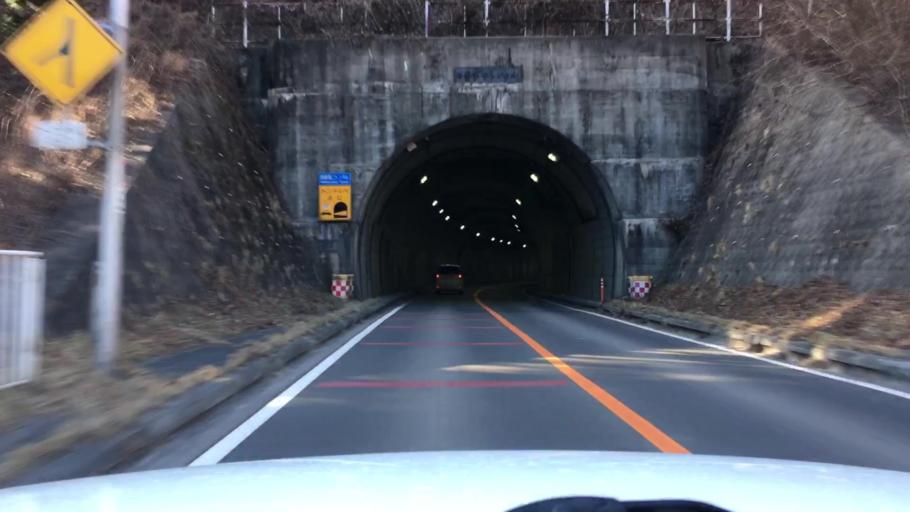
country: JP
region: Iwate
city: Miyako
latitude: 39.5978
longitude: 141.7415
